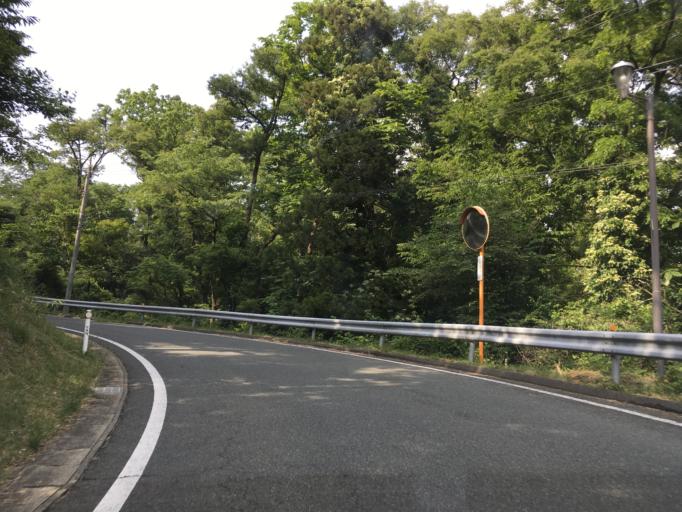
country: JP
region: Iwate
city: Hanamaki
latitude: 39.3993
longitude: 141.1661
